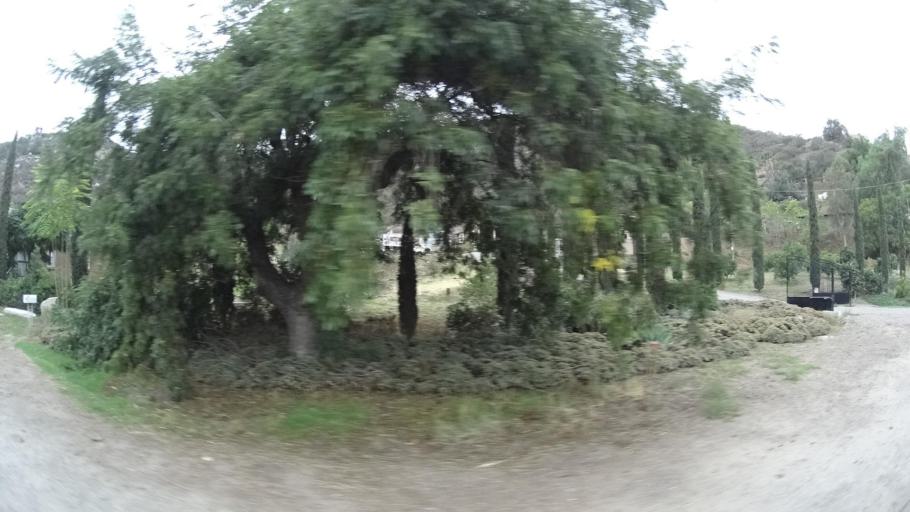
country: US
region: California
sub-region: San Diego County
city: Lakeside
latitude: 32.8759
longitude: -116.8667
